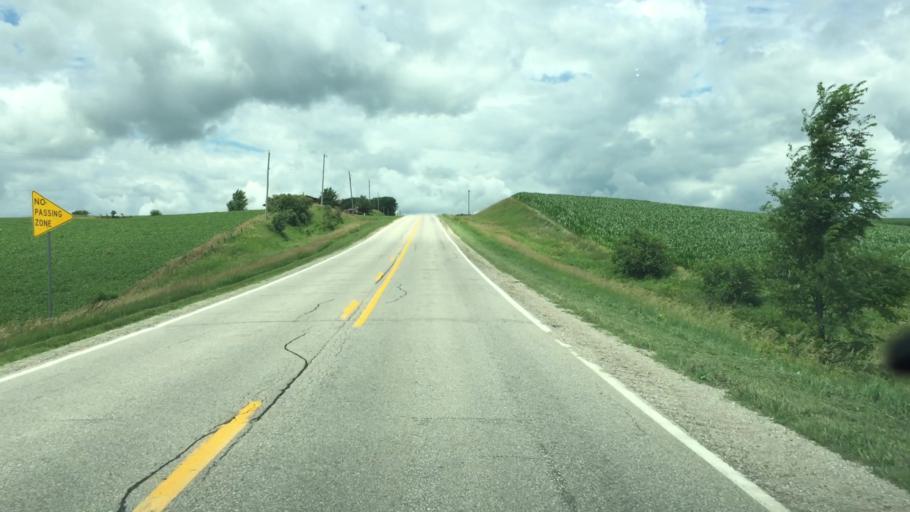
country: US
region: Iowa
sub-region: Jasper County
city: Monroe
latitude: 41.5736
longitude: -93.0796
